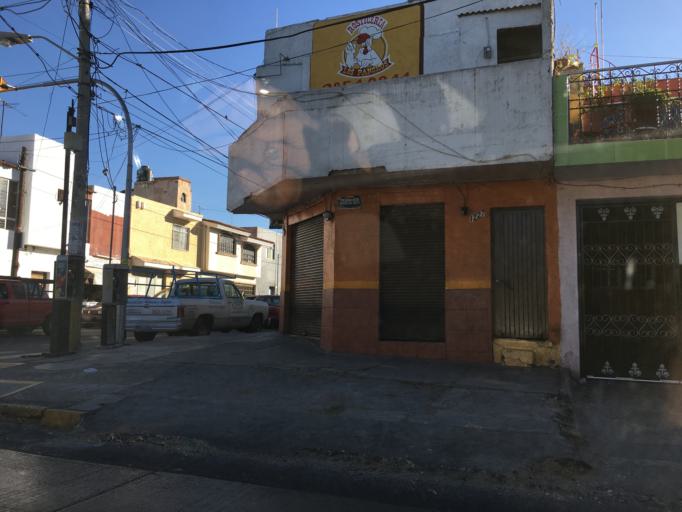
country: MX
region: Jalisco
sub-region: Zapopan
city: Zapopan
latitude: 20.7066
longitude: -103.3519
